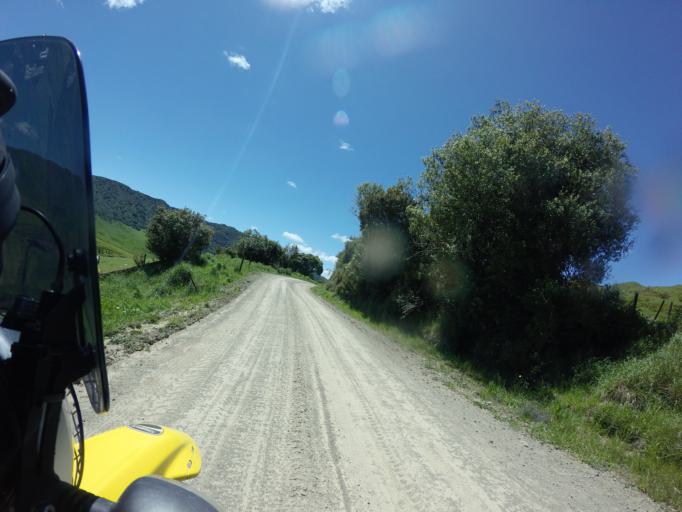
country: NZ
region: Bay of Plenty
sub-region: Opotiki District
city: Opotiki
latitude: -38.4073
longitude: 177.4463
